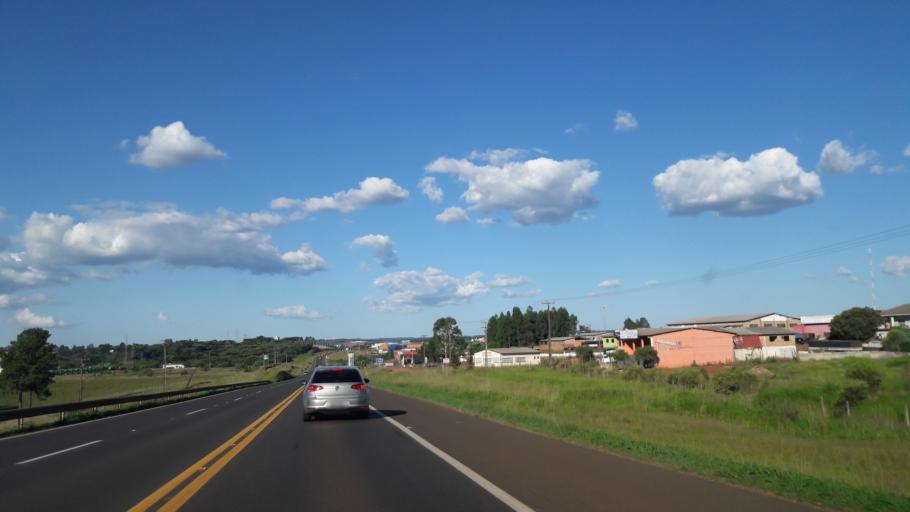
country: BR
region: Parana
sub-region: Guarapuava
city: Guarapuava
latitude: -25.3786
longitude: -51.5067
